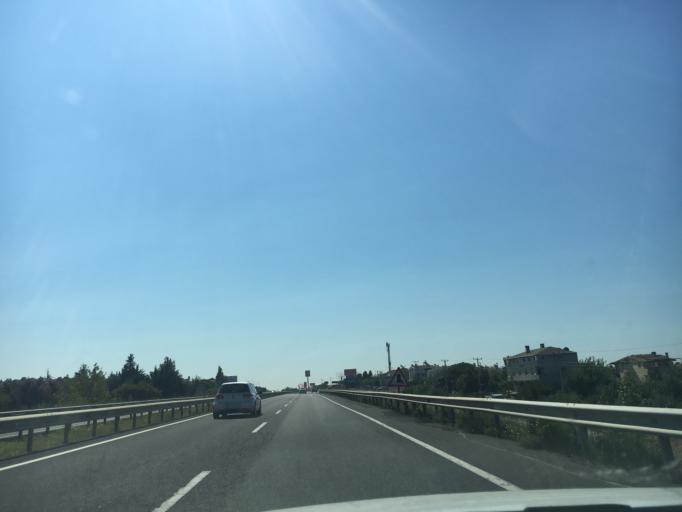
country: TR
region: Tekirdag
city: Marmara Ereglisi
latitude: 40.9740
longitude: 27.8779
